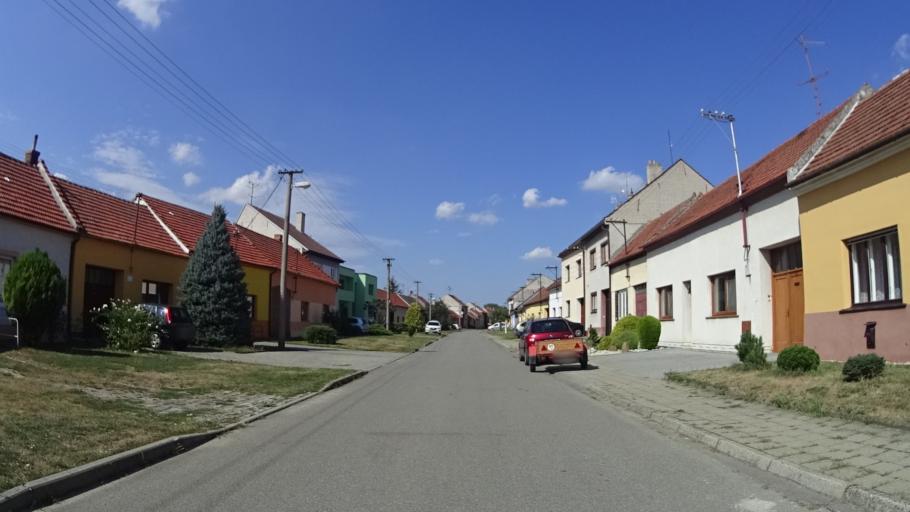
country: CZ
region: Zlin
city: Uhersky Ostroh
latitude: 48.9907
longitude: 17.4003
